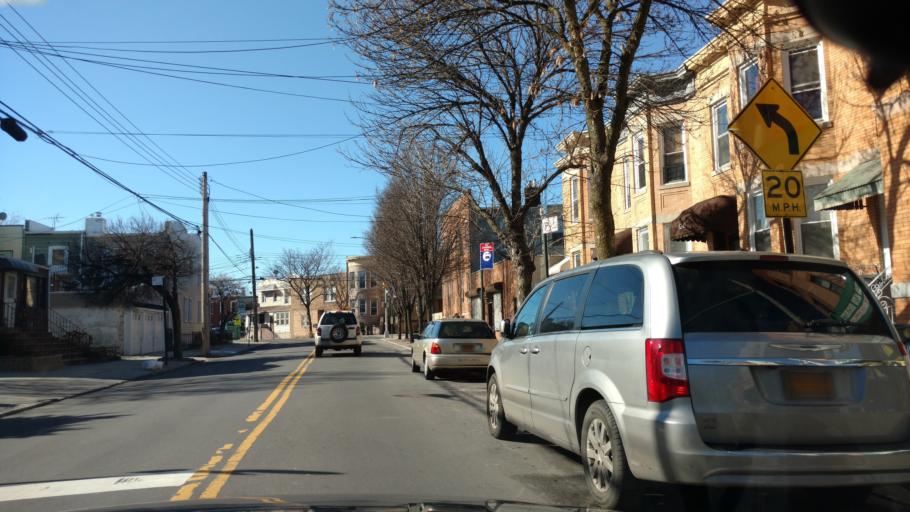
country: US
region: New York
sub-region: Kings County
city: East New York
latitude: 40.6979
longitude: -73.8921
